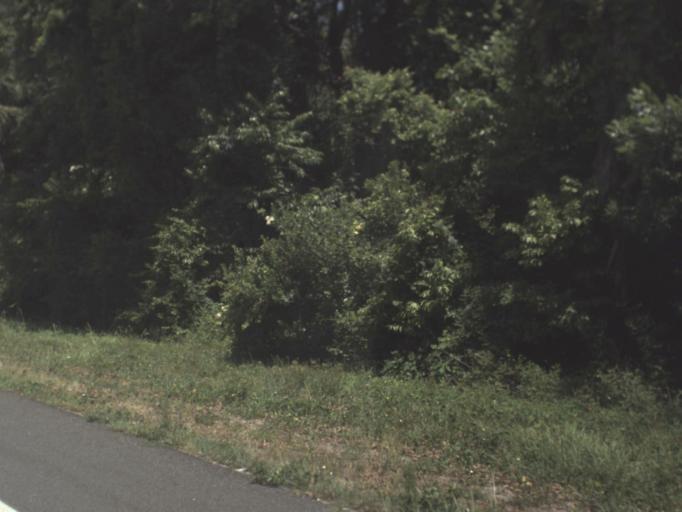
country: US
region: Florida
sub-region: Saint Johns County
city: Palm Valley
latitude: 30.1639
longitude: -81.3640
